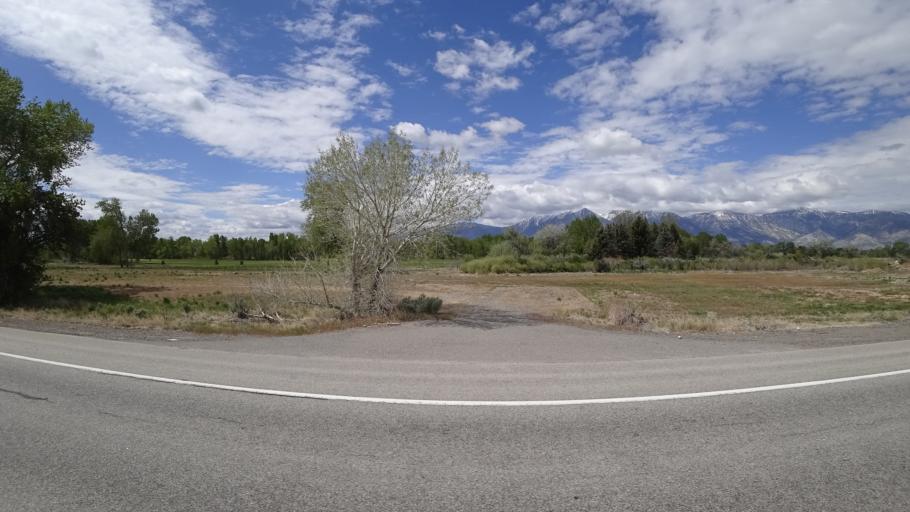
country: US
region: Nevada
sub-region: Douglas County
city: Gardnerville Ranchos
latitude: 38.9184
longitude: -119.7196
